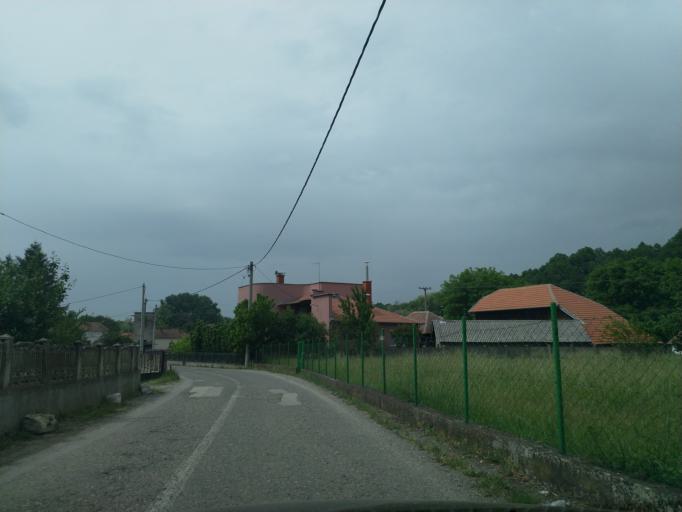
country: RS
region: Central Serbia
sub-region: Pomoravski Okrug
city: Paracin
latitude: 43.8590
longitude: 21.5926
